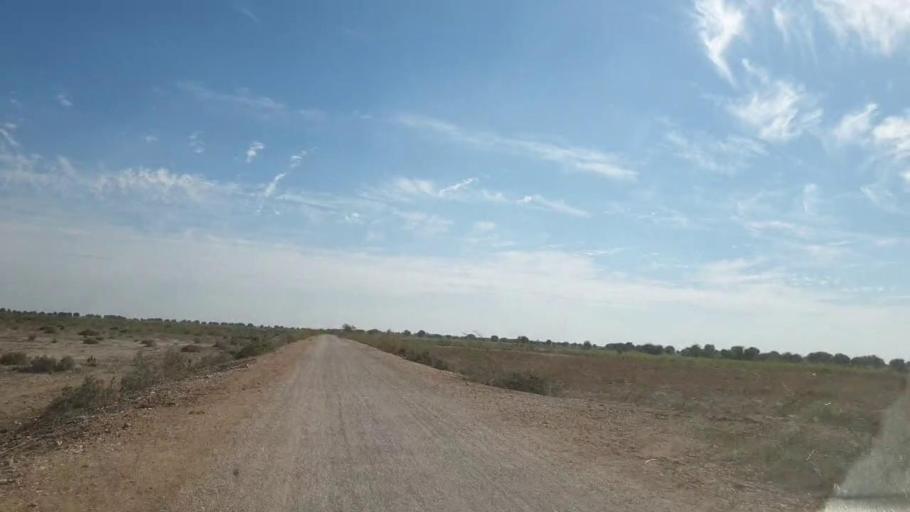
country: PK
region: Sindh
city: Pithoro
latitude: 25.5646
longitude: 69.3015
